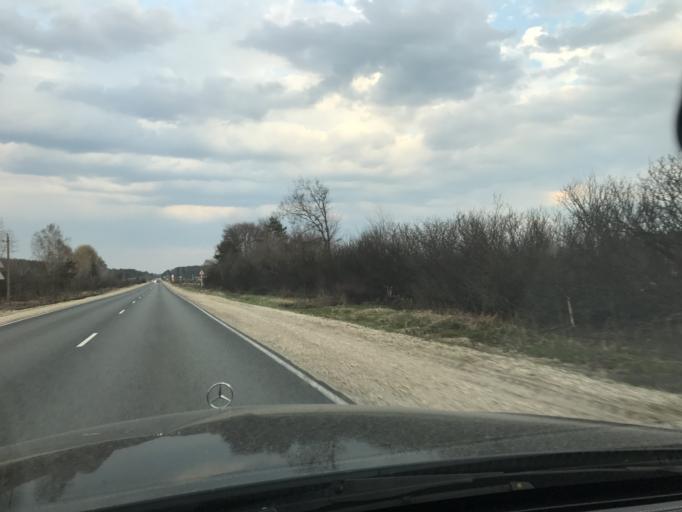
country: RU
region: Vladimir
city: Murom
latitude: 55.6259
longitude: 41.8898
